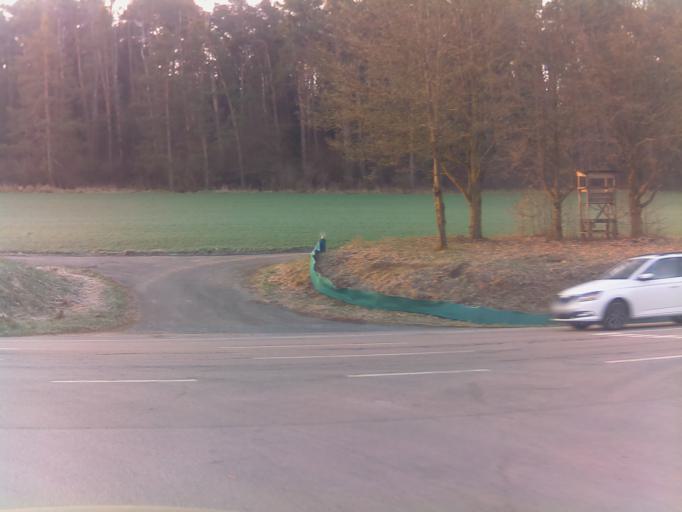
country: DE
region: Bavaria
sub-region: Upper Palatinate
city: Burglengenfeld
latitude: 49.1981
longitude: 12.0225
